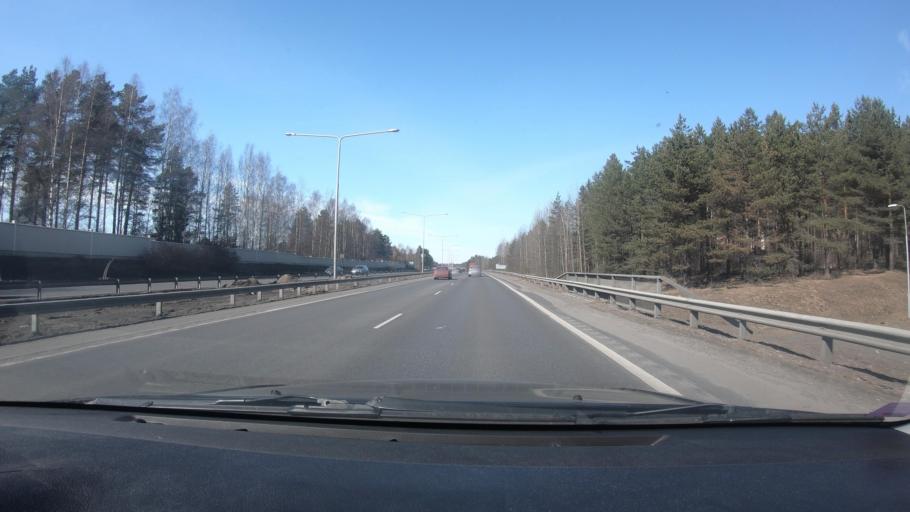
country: FI
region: Northern Ostrobothnia
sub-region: Oulu
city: Oulu
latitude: 65.0364
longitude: 25.4853
